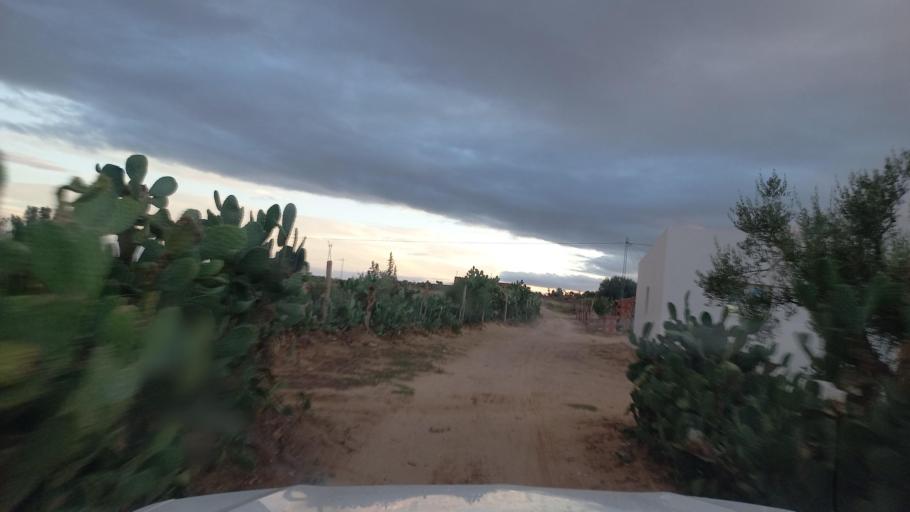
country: TN
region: Al Qasrayn
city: Kasserine
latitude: 35.2590
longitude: 8.9370
